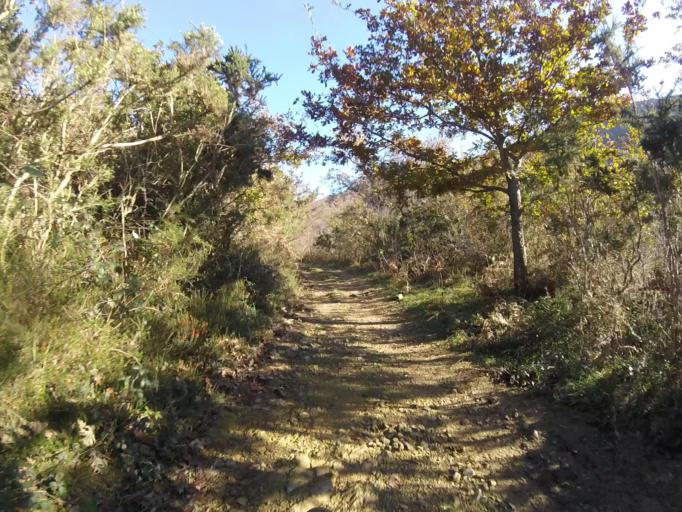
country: ES
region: Navarre
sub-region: Provincia de Navarra
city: Bera
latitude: 43.3140
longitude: -1.7247
